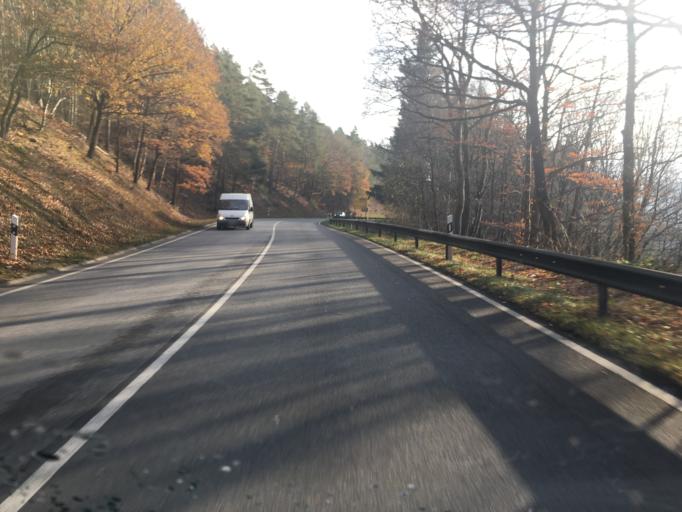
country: DE
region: North Rhine-Westphalia
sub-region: Regierungsbezirk Koln
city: Kall
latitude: 50.5577
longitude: 6.5409
